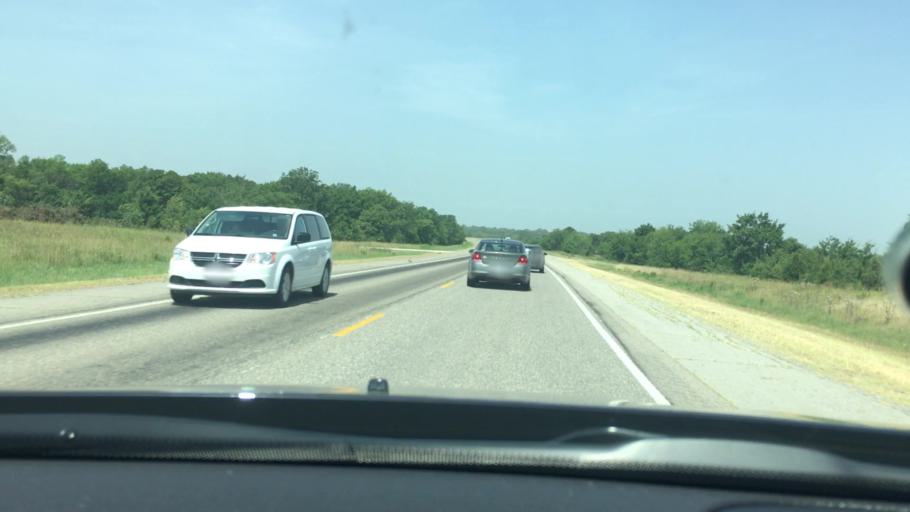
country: US
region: Oklahoma
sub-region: Coal County
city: Coalgate
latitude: 34.5991
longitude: -96.3178
